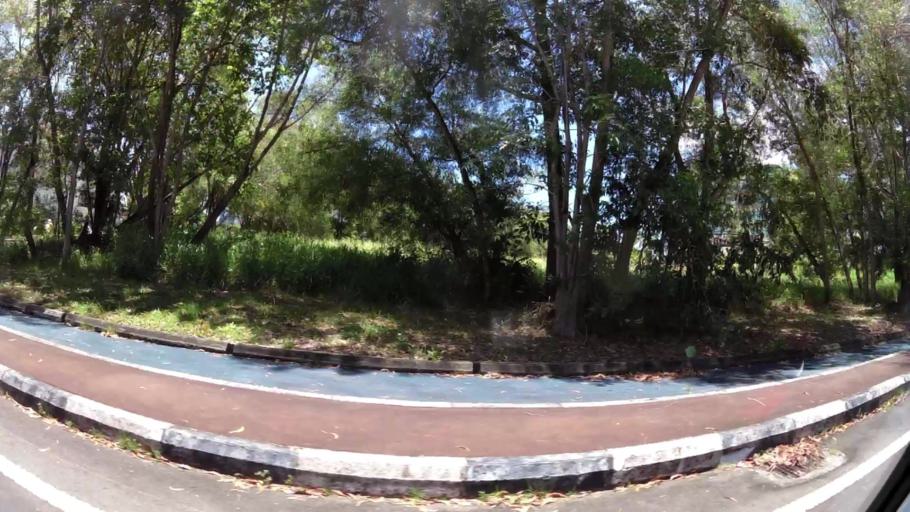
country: BN
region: Brunei and Muara
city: Bandar Seri Begawan
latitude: 4.9181
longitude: 114.9431
